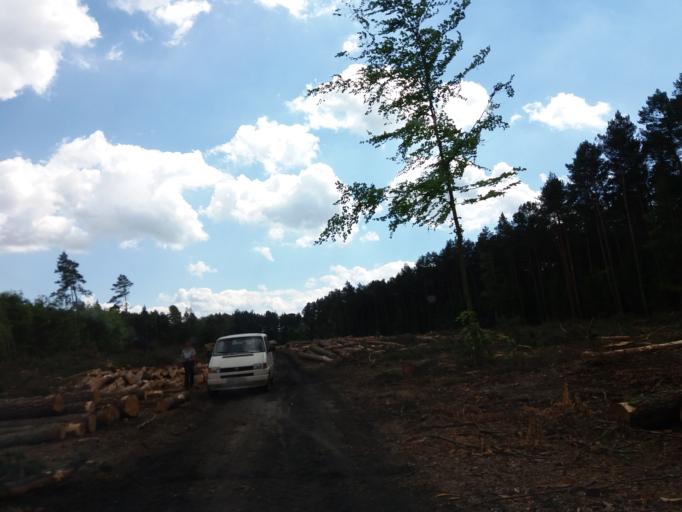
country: PL
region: West Pomeranian Voivodeship
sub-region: Powiat choszczenski
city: Drawno
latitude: 53.2330
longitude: 15.7887
